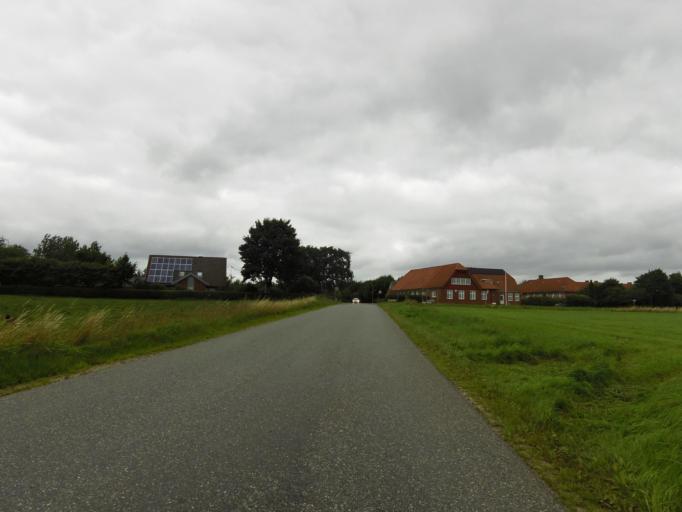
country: DK
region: South Denmark
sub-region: Haderslev Kommune
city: Gram
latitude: 55.2682
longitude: 9.1697
